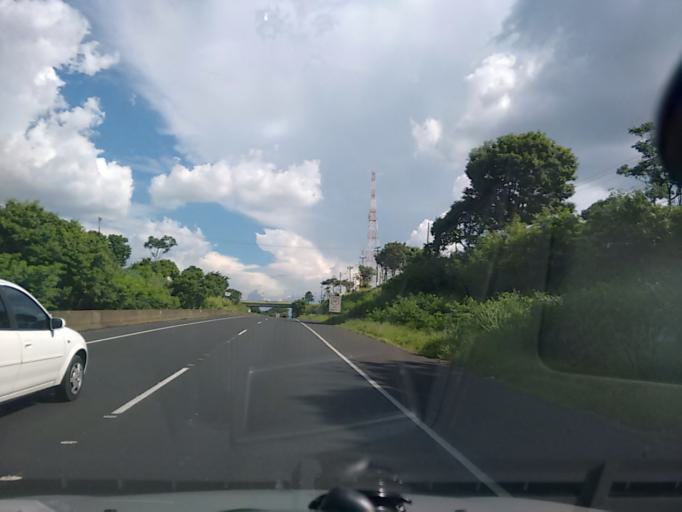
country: BR
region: Sao Paulo
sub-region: Marilia
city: Marilia
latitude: -22.2043
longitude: -49.9640
